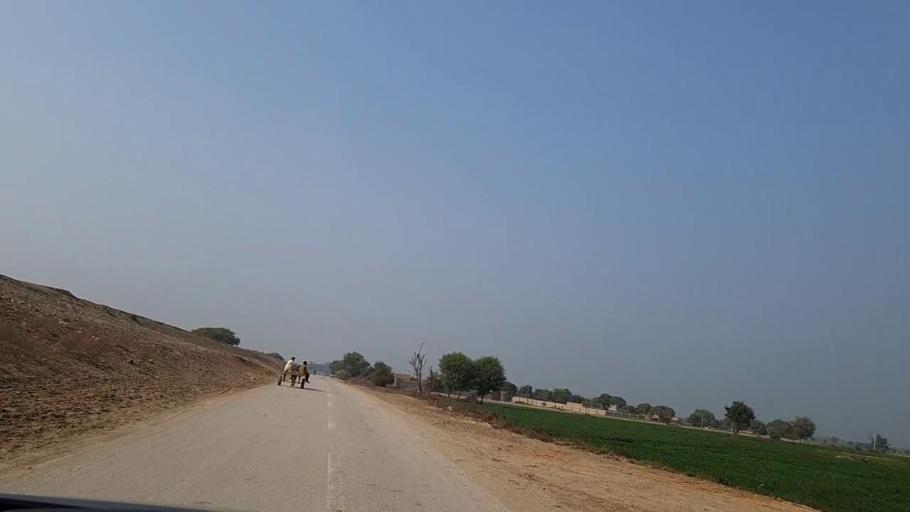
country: PK
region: Sindh
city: Sann
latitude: 26.1575
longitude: 68.1169
